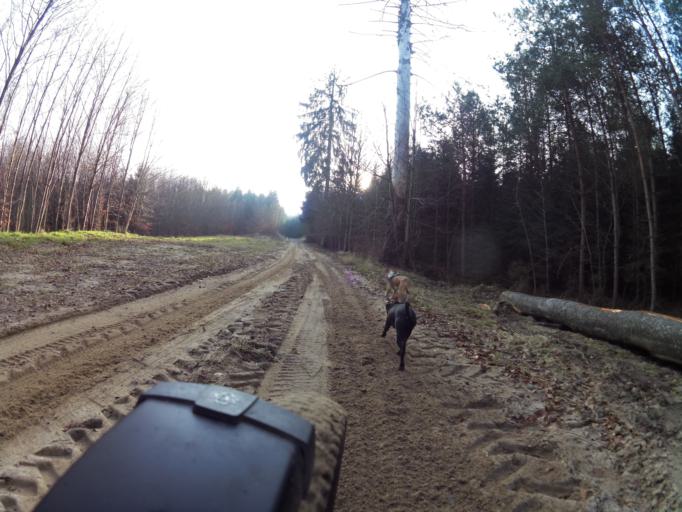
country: PL
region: West Pomeranian Voivodeship
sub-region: Powiat koszalinski
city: Polanow
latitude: 54.1801
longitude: 16.7207
